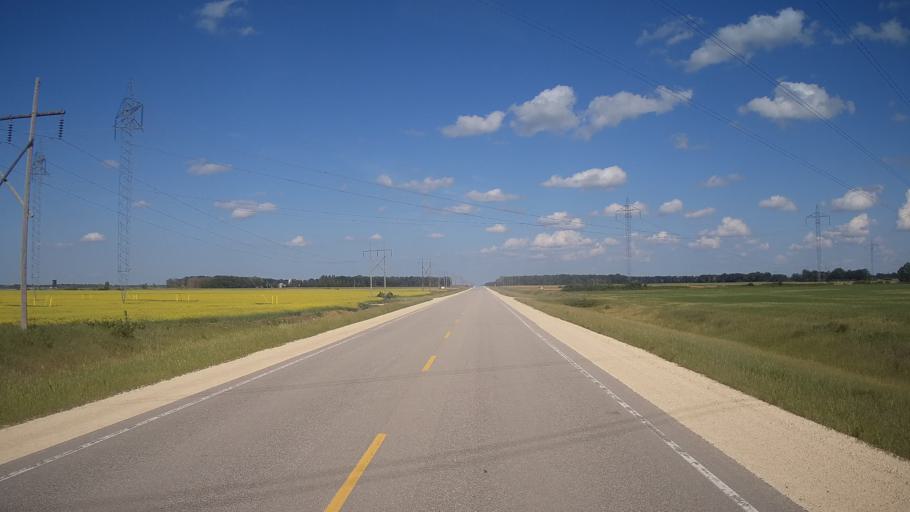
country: CA
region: Manitoba
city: Stonewall
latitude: 50.1227
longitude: -97.4912
